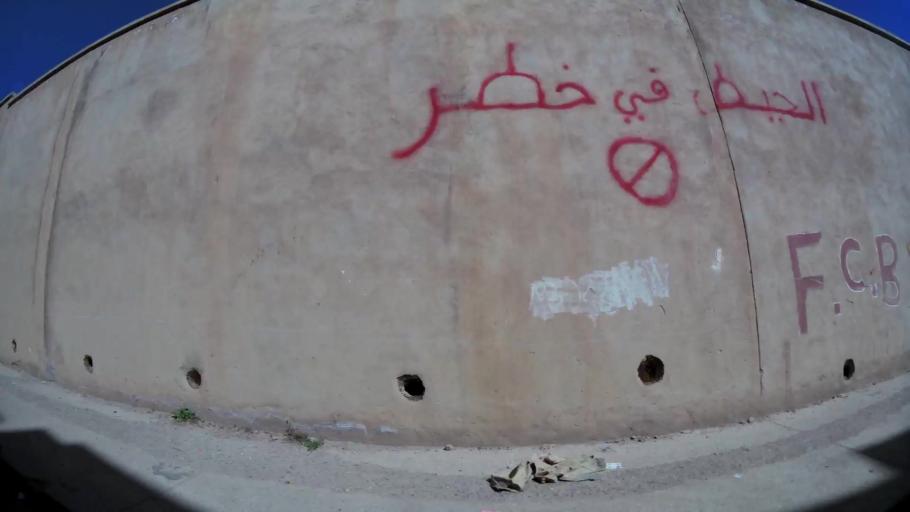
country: MA
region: Oriental
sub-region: Oujda-Angad
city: Oujda
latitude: 34.6582
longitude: -1.9495
